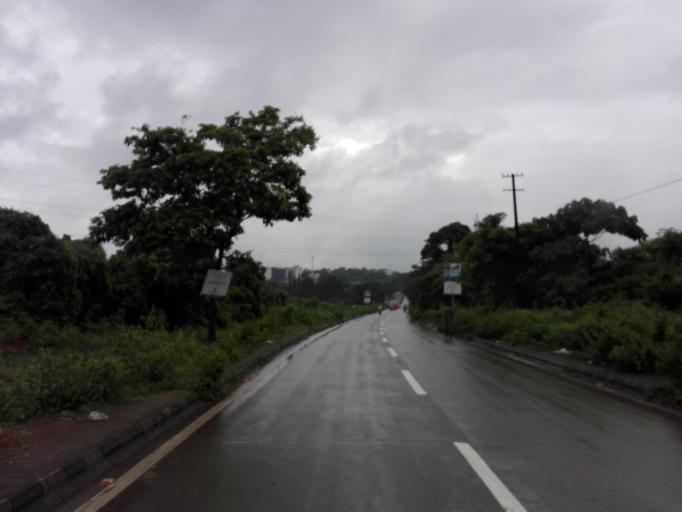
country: IN
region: Kerala
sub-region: Ernakulam
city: Aluva
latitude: 10.0516
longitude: 76.3480
